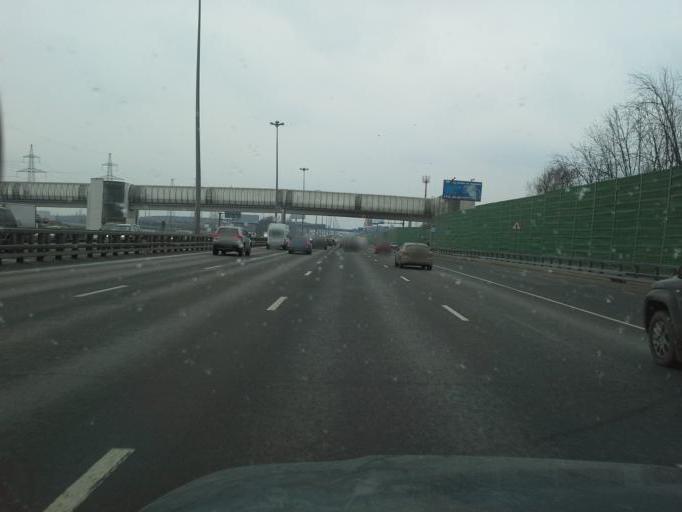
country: RU
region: Moskovskaya
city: Mosrentgen
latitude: 55.6301
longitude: 37.4345
